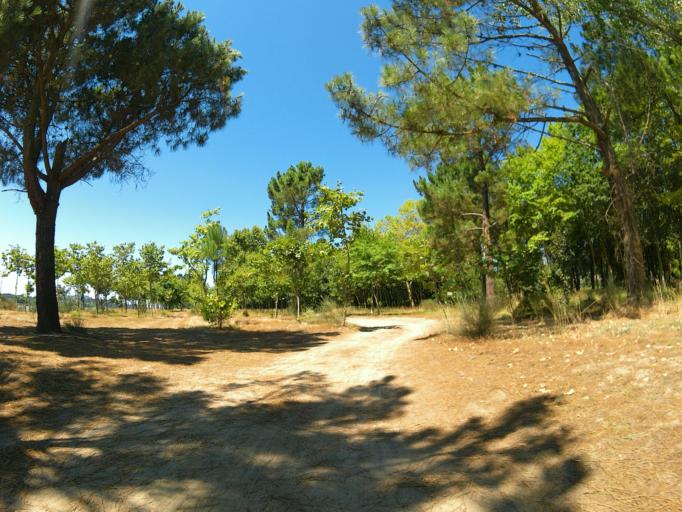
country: PT
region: Viana do Castelo
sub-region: Viana do Castelo
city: Darque
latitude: 41.7047
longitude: -8.7307
